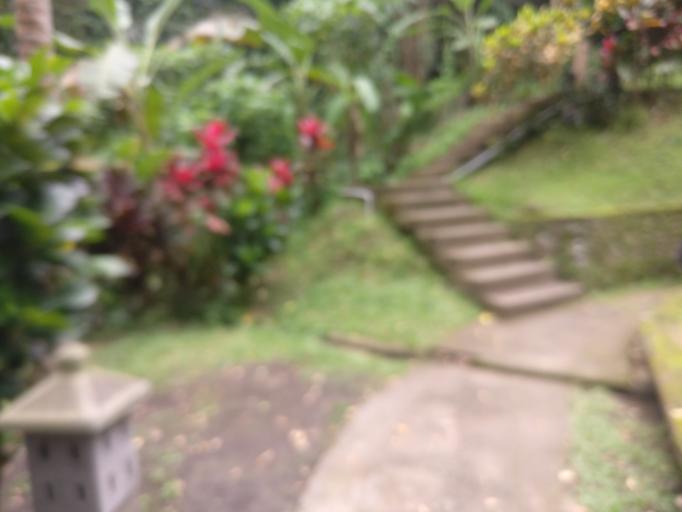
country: ID
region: Bali
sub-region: Kabupaten Gianyar
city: Ubud
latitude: -8.5238
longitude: 115.2862
